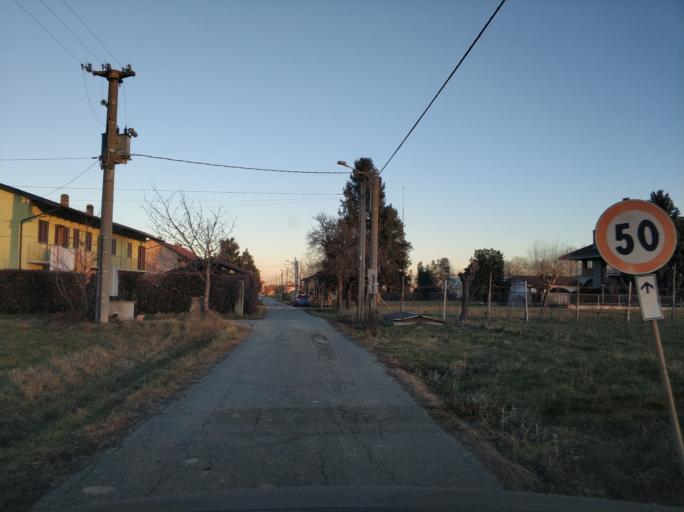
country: IT
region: Piedmont
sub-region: Provincia di Torino
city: Vauda Canavese Superiore
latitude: 45.2658
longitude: 7.6356
